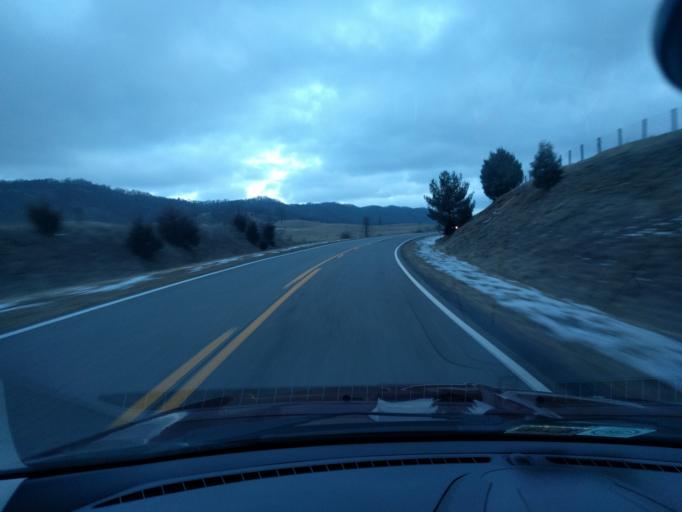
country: US
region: Virginia
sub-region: Alleghany County
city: Clifton Forge
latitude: 37.9111
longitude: -79.8972
